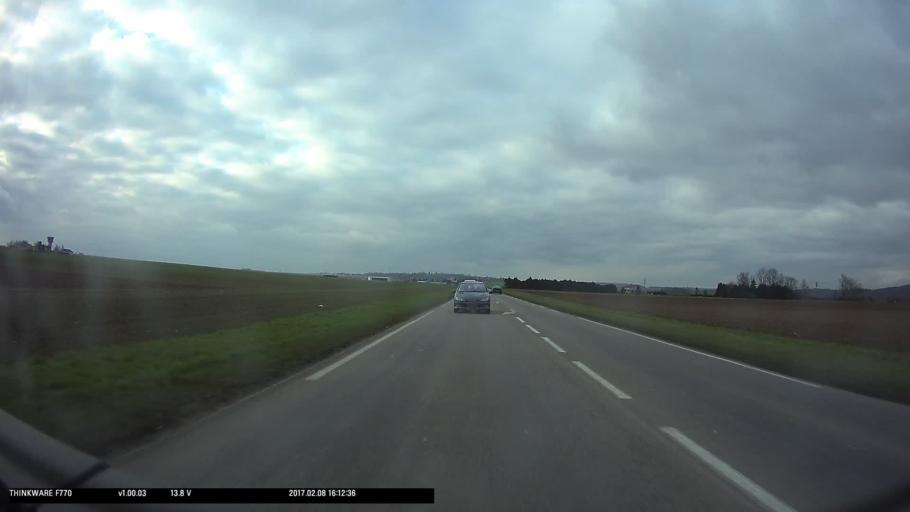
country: FR
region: Ile-de-France
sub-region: Departement du Val-d'Oise
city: Osny
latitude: 49.0940
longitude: 2.0527
